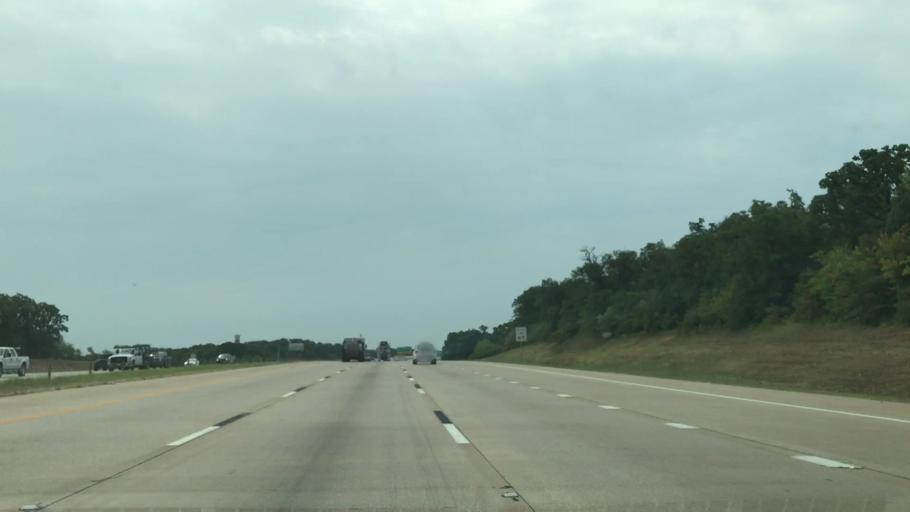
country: US
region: Texas
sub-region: Denton County
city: Trophy Club
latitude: 32.9780
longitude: -97.1640
